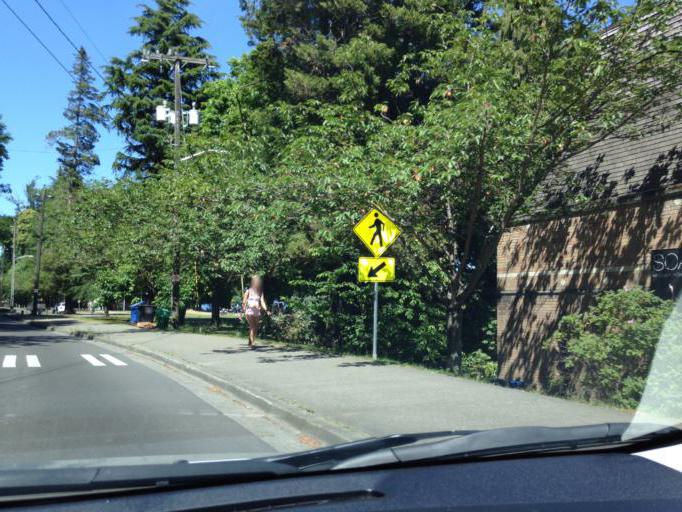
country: US
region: Washington
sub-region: King County
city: Seattle
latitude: 47.6092
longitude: -122.2830
